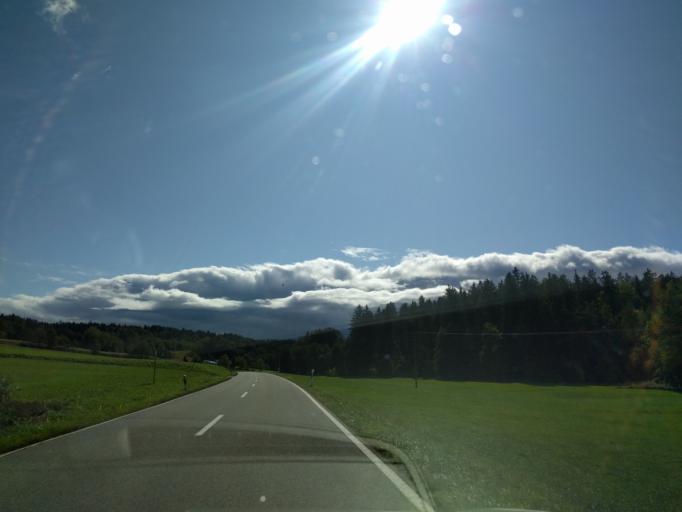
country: DE
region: Bavaria
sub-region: Lower Bavaria
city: Hengersberg
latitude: 48.8036
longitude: 13.0482
